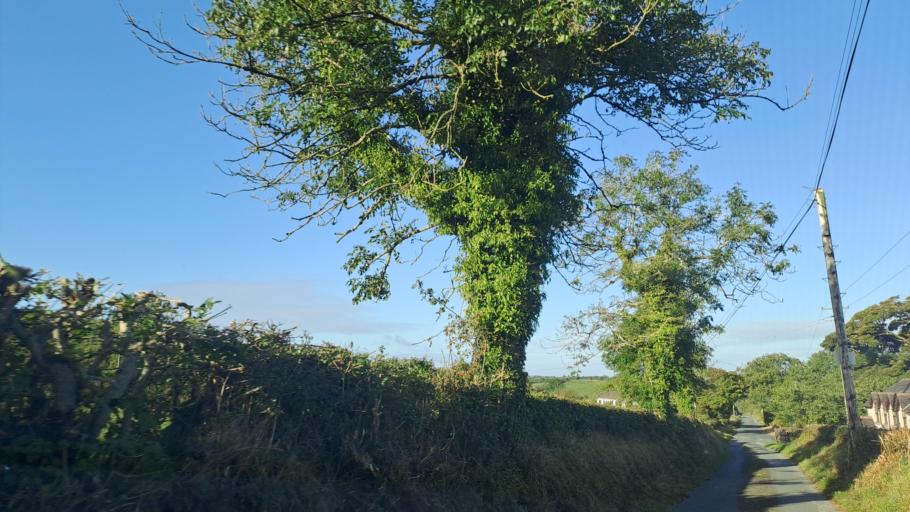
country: IE
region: Ulster
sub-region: An Cabhan
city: Kingscourt
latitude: 53.9884
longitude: -6.8559
